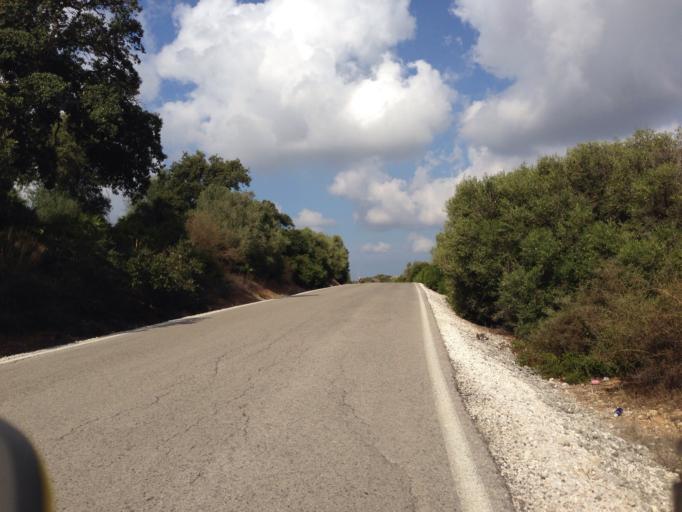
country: ES
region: Andalusia
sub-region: Provincia de Cadiz
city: Conil de la Frontera
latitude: 36.3425
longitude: -6.0301
